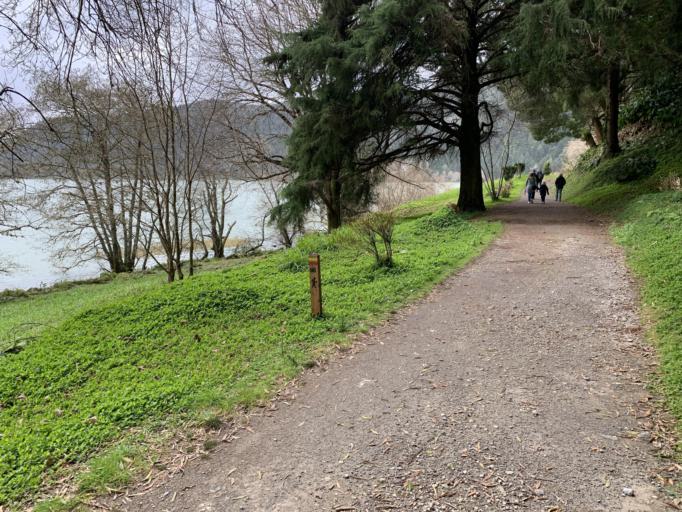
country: PT
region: Azores
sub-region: Povoacao
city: Furnas
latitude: 37.7641
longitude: -25.3364
